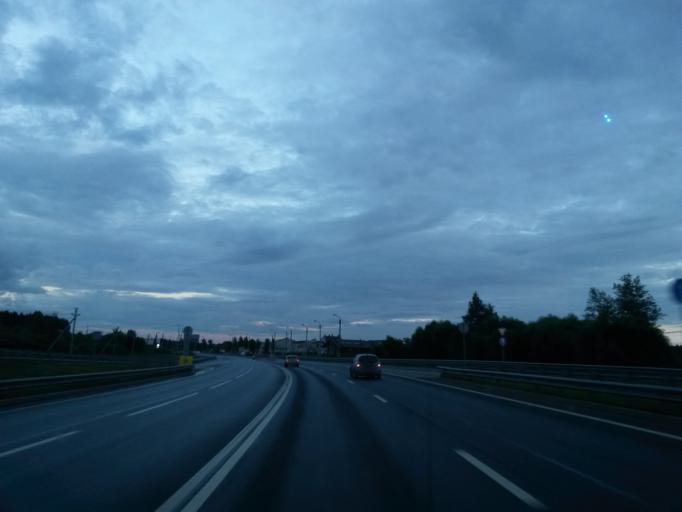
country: RU
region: Jaroslavl
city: Yaroslavl
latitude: 57.6809
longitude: 39.8985
